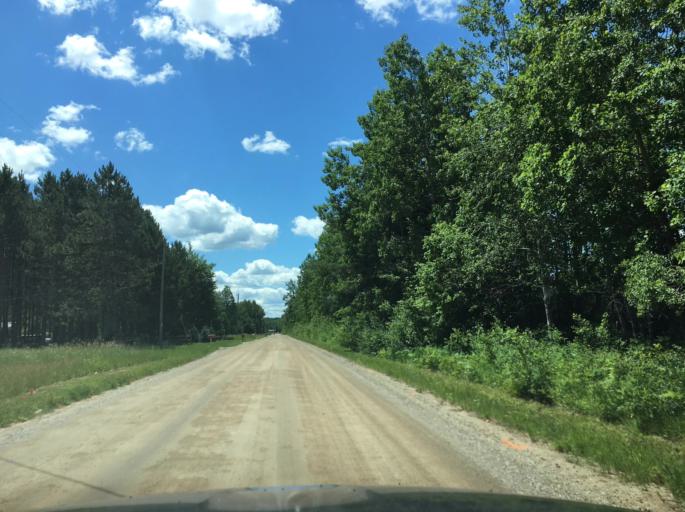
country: US
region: Michigan
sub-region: Osceola County
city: Reed City
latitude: 43.8725
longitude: -85.3887
